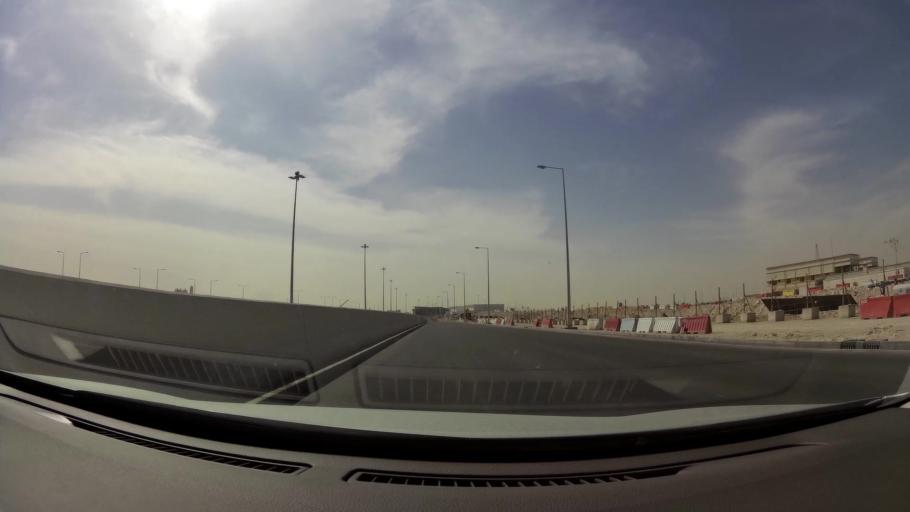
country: QA
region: Baladiyat ar Rayyan
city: Ar Rayyan
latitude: 25.3010
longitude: 51.4282
